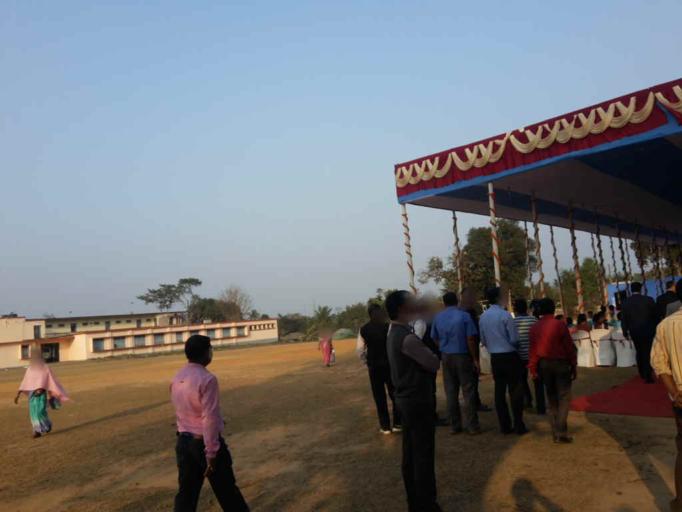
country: IN
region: Tripura
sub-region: West Tripura
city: Agartala
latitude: 23.8581
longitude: 91.2976
